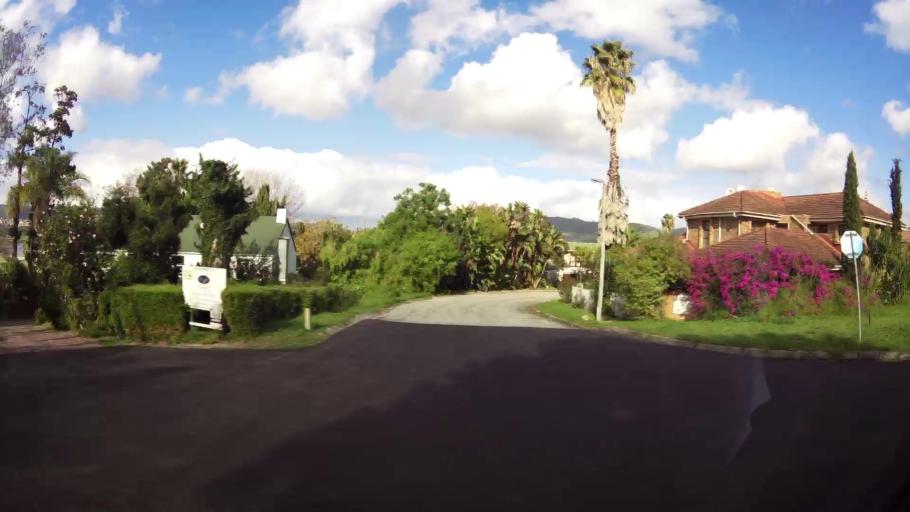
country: ZA
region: Western Cape
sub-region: Eden District Municipality
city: Knysna
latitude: -34.0384
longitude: 23.0620
